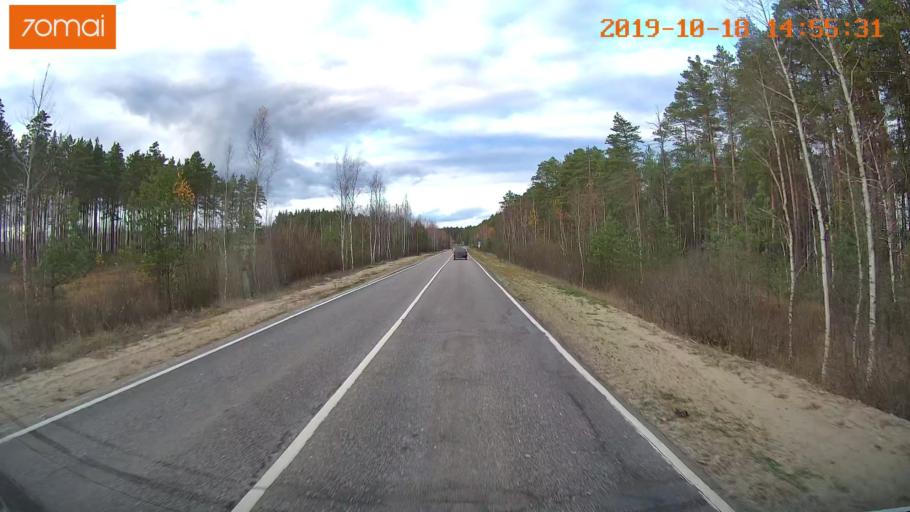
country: RU
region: Vladimir
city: Kurlovo
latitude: 55.4534
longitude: 40.5890
